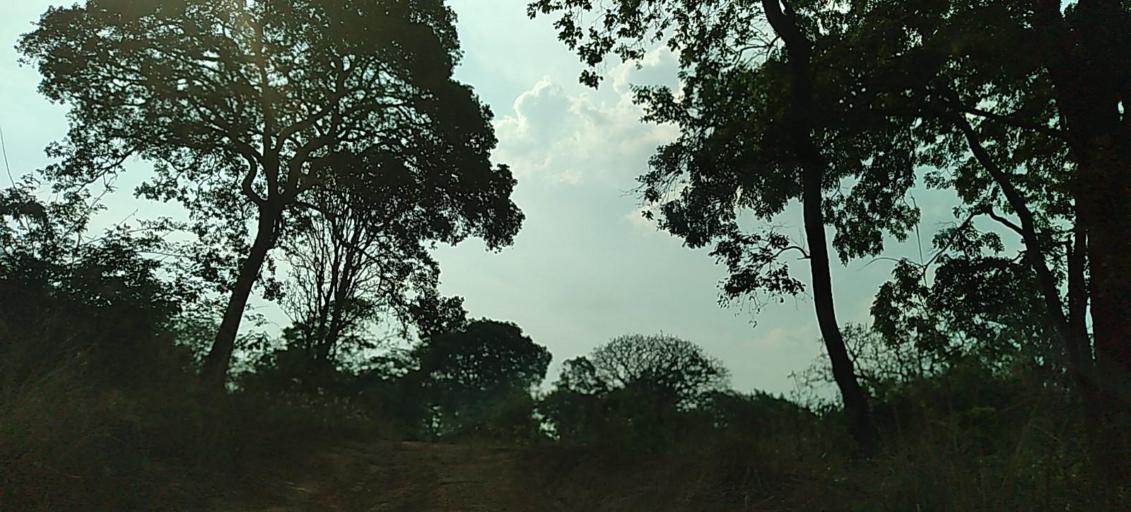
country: ZM
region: North-Western
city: Solwezi
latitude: -12.0653
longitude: 26.1769
